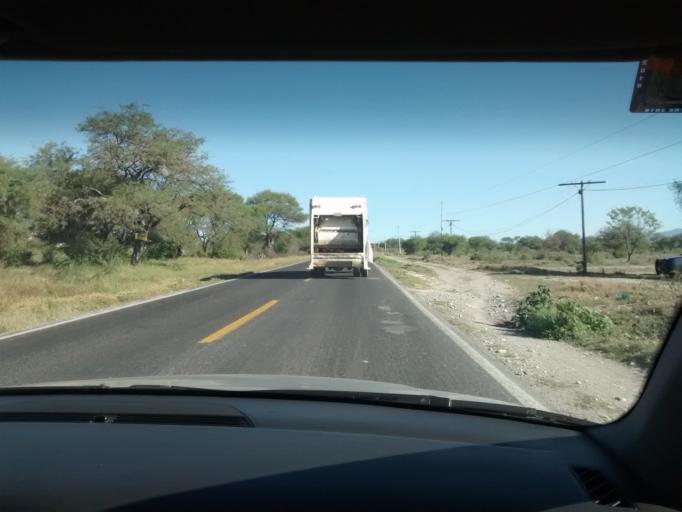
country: MX
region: Puebla
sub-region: Tepanco de Lopez
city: San Andres Cacaloapan
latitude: 18.5676
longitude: -97.5723
